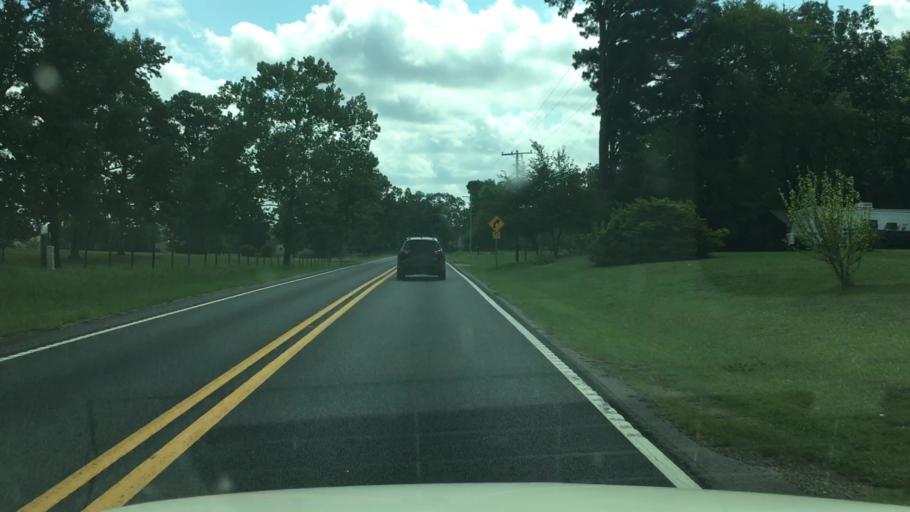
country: US
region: Arkansas
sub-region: Garland County
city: Lake Hamilton
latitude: 34.2649
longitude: -93.1350
